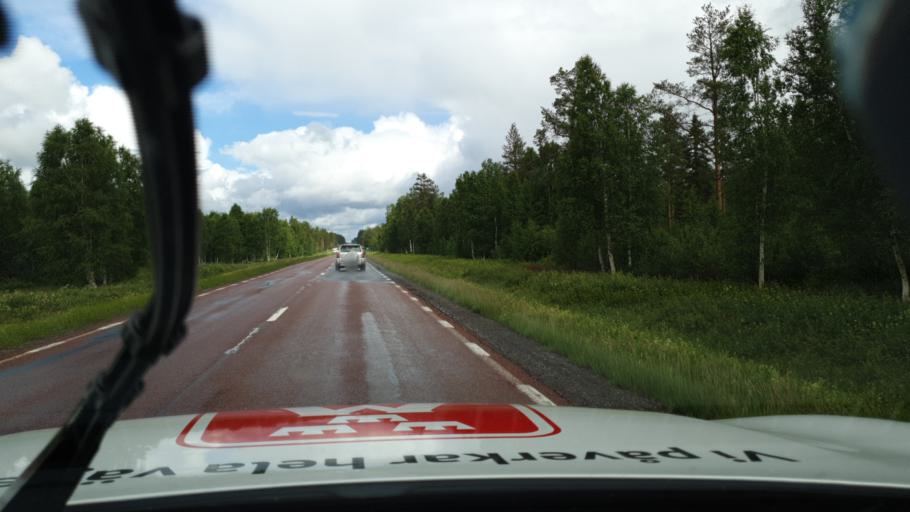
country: SE
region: Jaemtland
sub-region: Stroemsunds Kommun
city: Stroemsund
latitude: 63.7541
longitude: 15.4978
